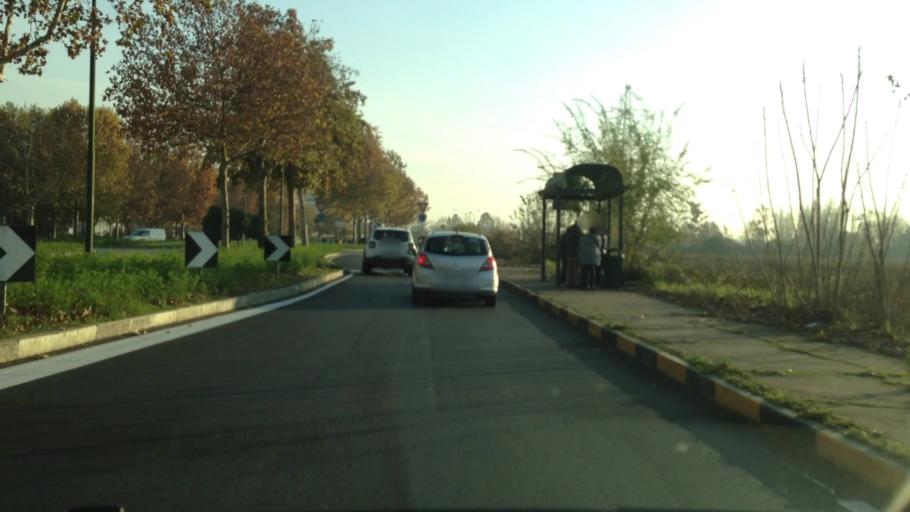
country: IT
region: Piedmont
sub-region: Provincia di Torino
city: Savonera
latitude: 45.1012
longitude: 7.6251
